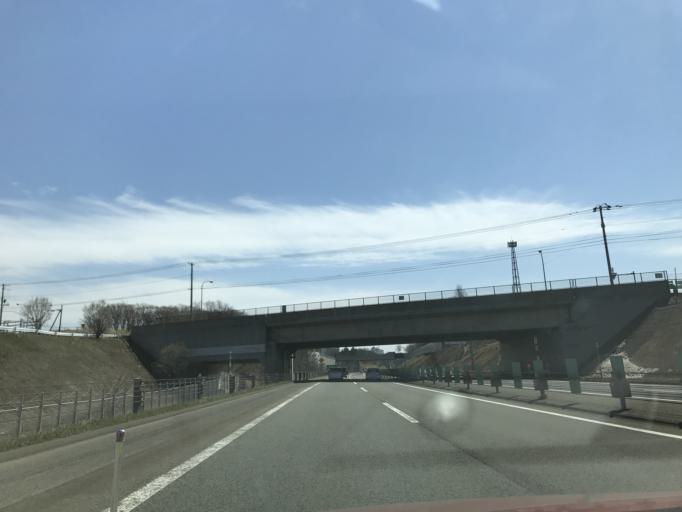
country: JP
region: Hokkaido
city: Ebetsu
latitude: 43.0924
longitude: 141.5018
